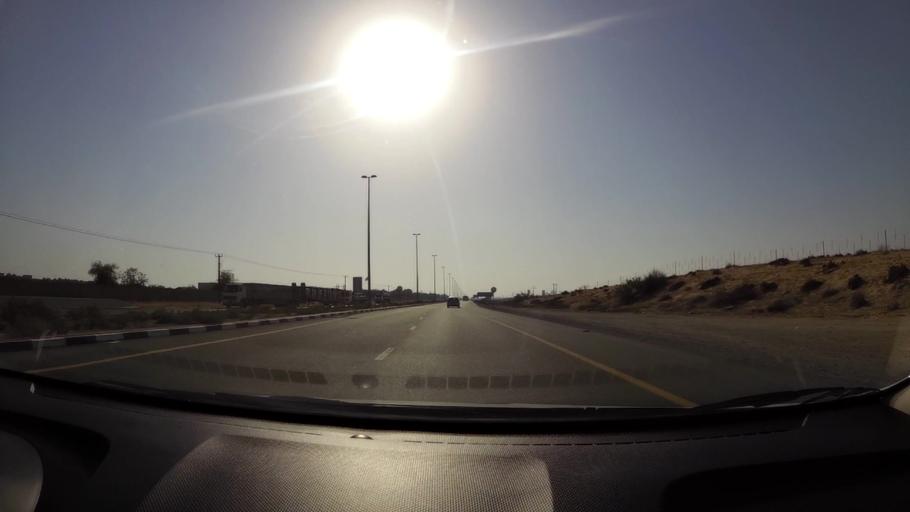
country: AE
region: Umm al Qaywayn
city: Umm al Qaywayn
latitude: 25.4296
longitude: 55.5830
